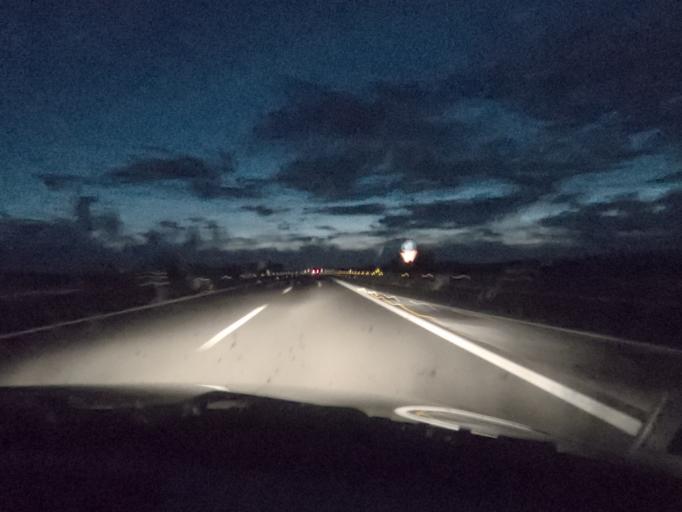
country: ES
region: Extremadura
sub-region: Provincia de Caceres
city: Morcillo
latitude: 39.9807
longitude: -6.3890
